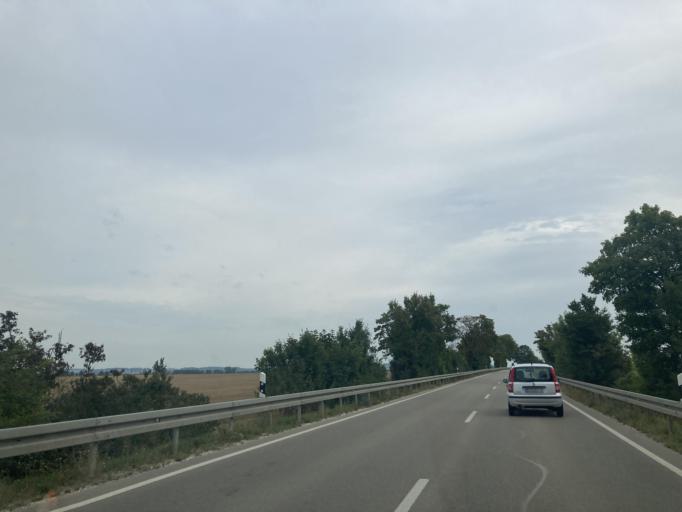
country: DE
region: Bavaria
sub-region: Swabia
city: Munningen
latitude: 48.9144
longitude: 10.5682
